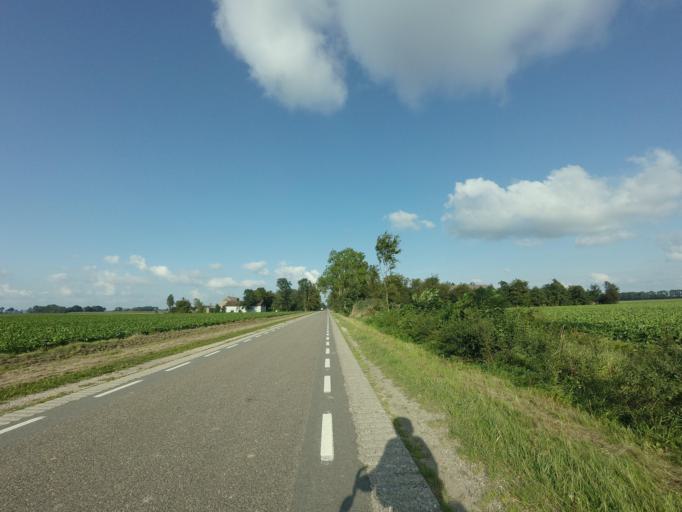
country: NL
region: Flevoland
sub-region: Gemeente Noordoostpolder
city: Ens
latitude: 52.6763
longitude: 5.8139
